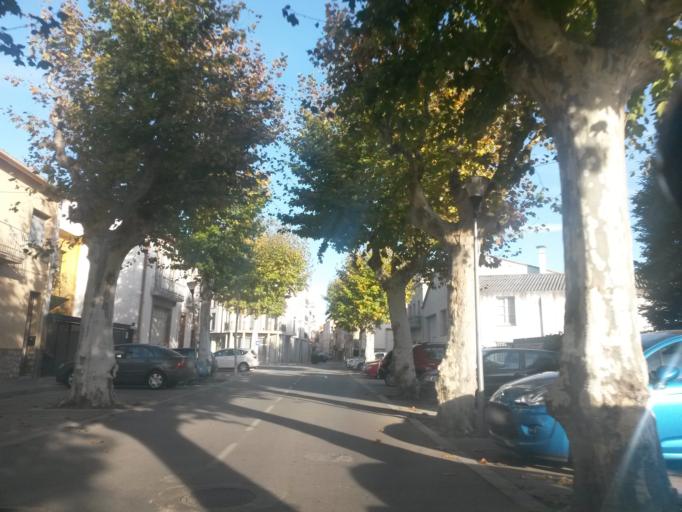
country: ES
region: Catalonia
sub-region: Provincia de Girona
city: Banyoles
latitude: 42.1167
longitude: 2.7589
